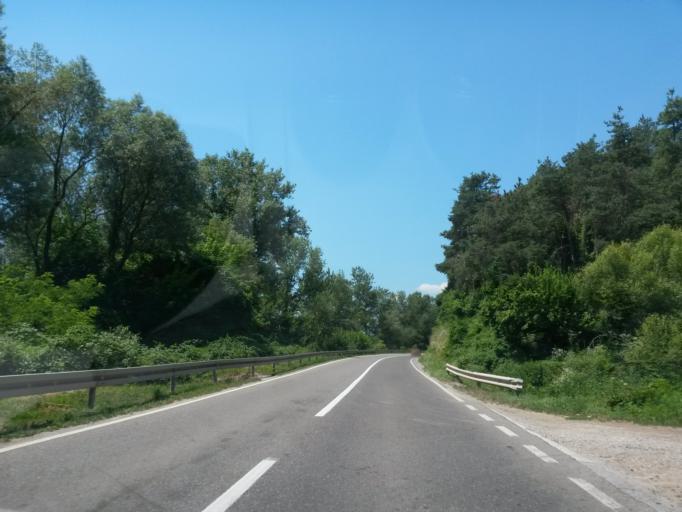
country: BA
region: Federation of Bosnia and Herzegovina
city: Odzak
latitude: 44.9705
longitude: 18.2698
